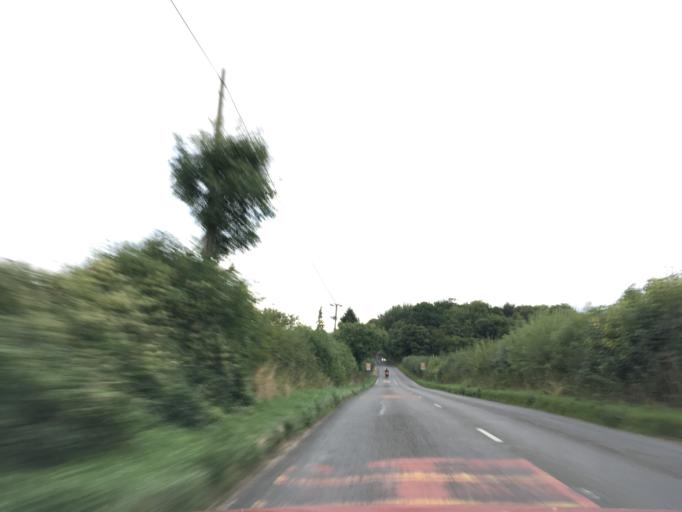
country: GB
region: England
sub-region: Wiltshire
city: Bremhill
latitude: 51.4266
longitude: -2.0627
